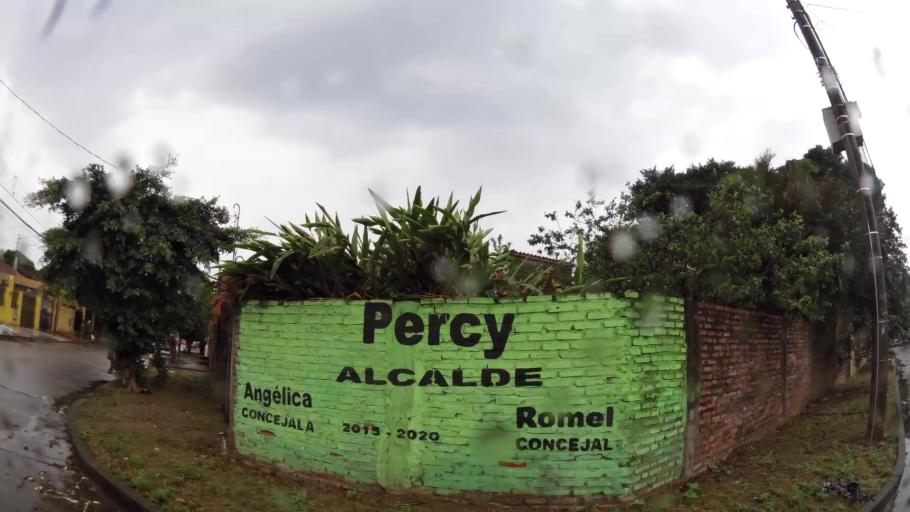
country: BO
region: Santa Cruz
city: Santa Cruz de la Sierra
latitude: -17.7954
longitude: -63.1544
